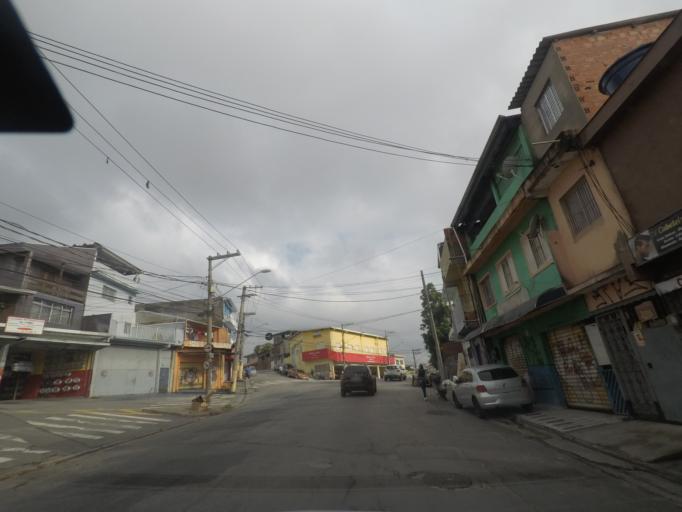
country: BR
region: Sao Paulo
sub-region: Osasco
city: Osasco
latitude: -23.5750
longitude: -46.7799
